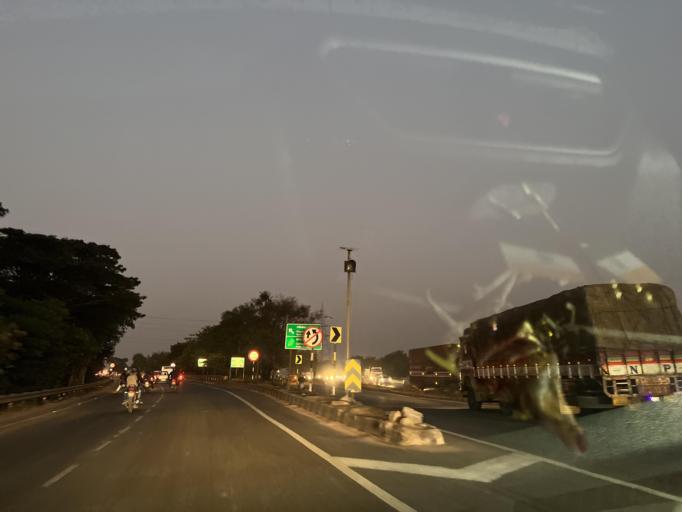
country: IN
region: Odisha
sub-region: Cuttack
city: Cuttack
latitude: 20.4364
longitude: 85.8853
